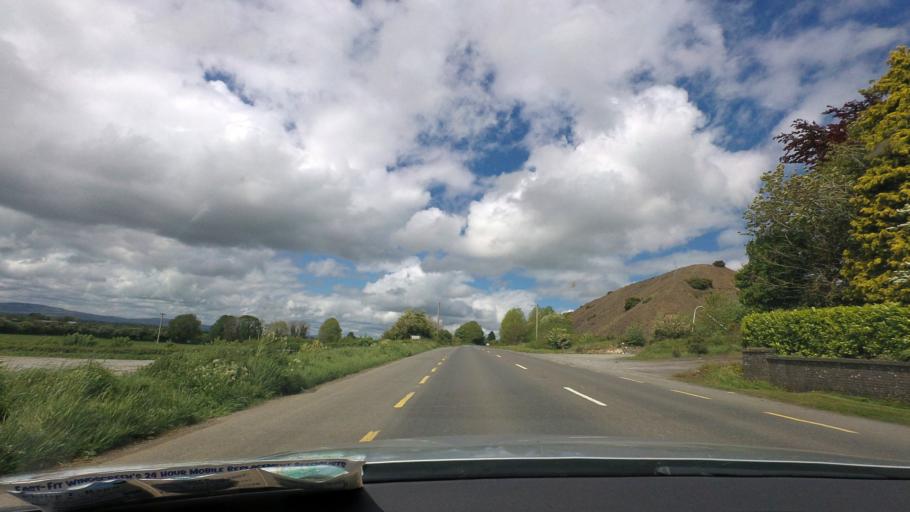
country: IE
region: Munster
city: Cashel
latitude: 52.5315
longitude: -7.8782
